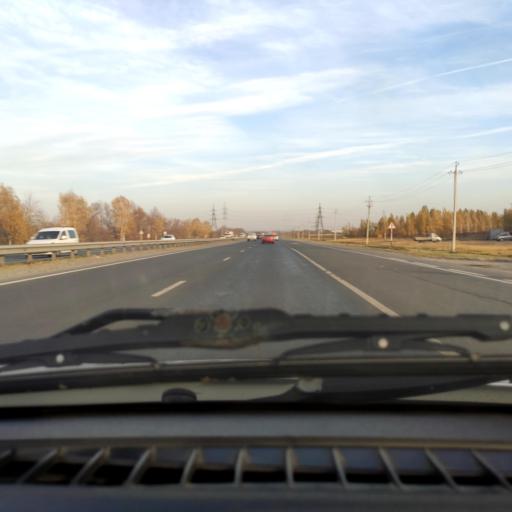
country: RU
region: Samara
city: Tol'yatti
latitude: 53.5770
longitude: 49.4260
